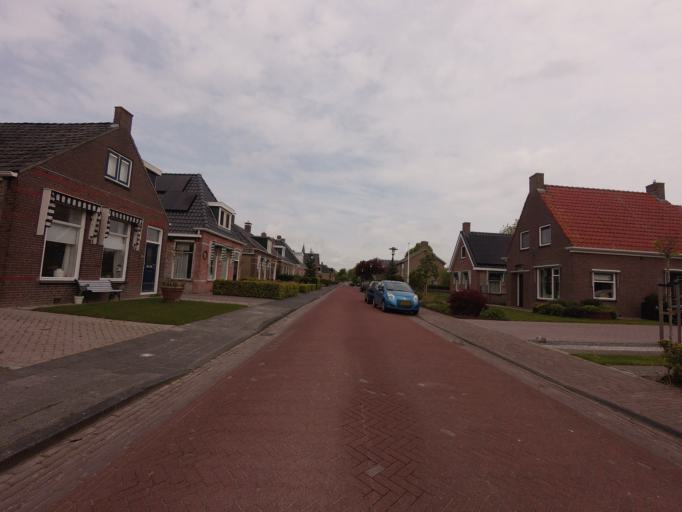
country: NL
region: Friesland
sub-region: Sudwest Fryslan
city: Bolsward
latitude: 53.0814
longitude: 5.4826
